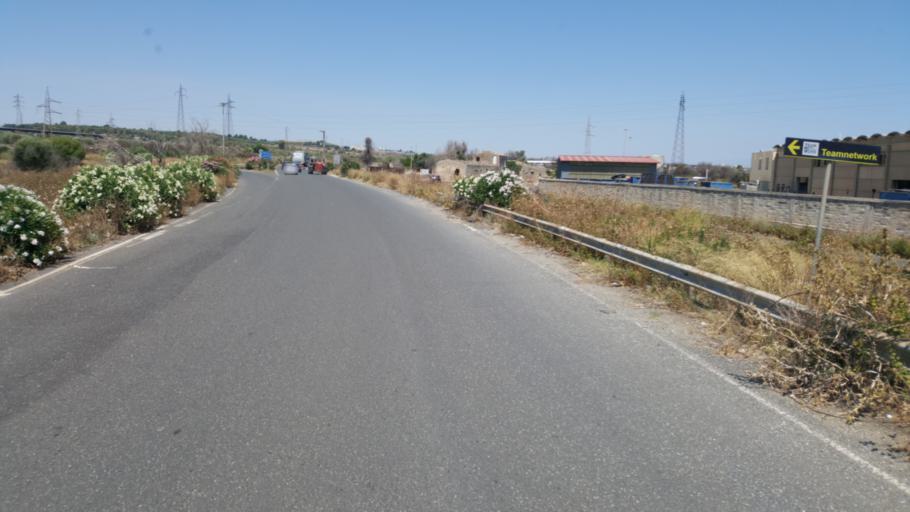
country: IT
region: Sicily
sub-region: Provincia di Siracusa
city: Melilli
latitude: 37.2022
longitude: 15.1629
